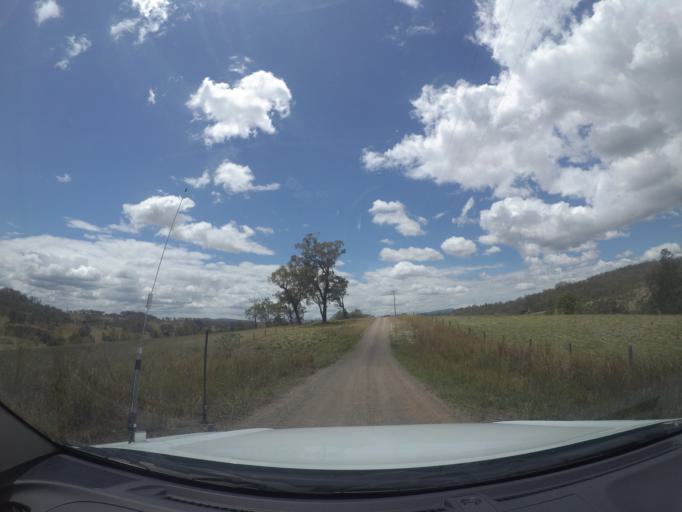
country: AU
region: Queensland
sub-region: Logan
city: Cedar Vale
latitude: -27.9089
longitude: 153.0556
